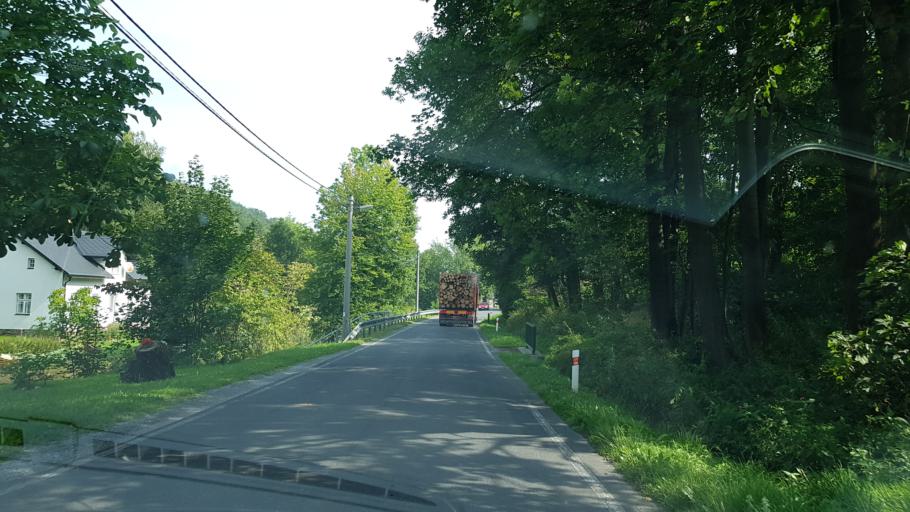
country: CZ
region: Olomoucky
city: Zlate Hory
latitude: 50.2408
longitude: 17.3473
